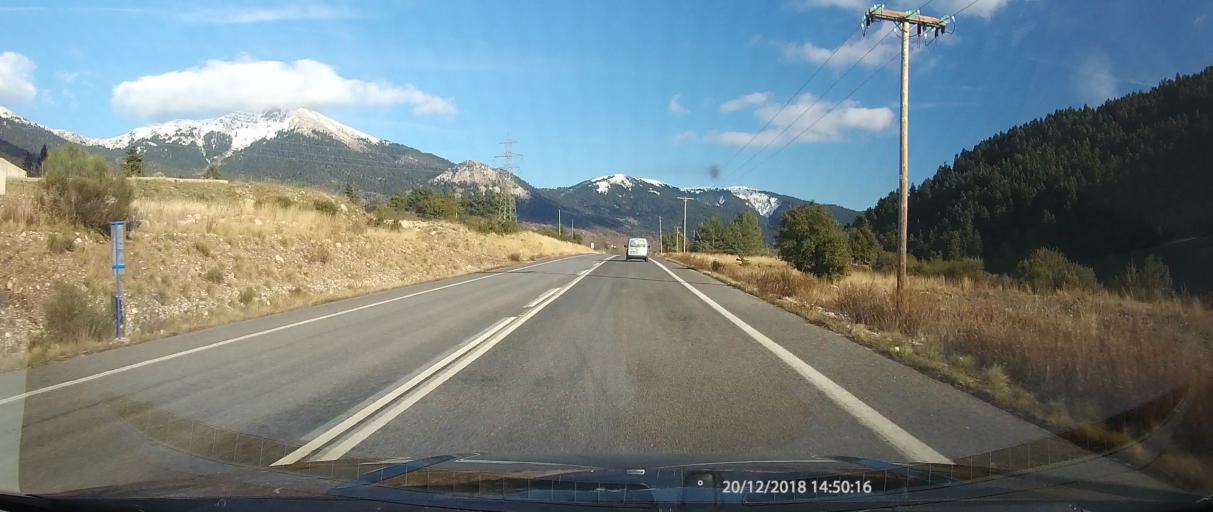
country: GR
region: Central Greece
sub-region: Nomos Evrytanias
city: Karpenisi
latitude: 38.9057
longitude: 21.8215
